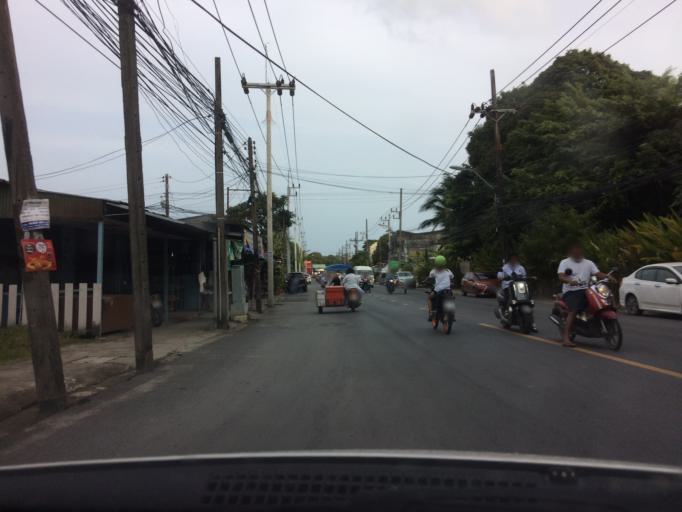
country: TH
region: Phuket
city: Ban Talat Yai
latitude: 7.8874
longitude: 98.4039
